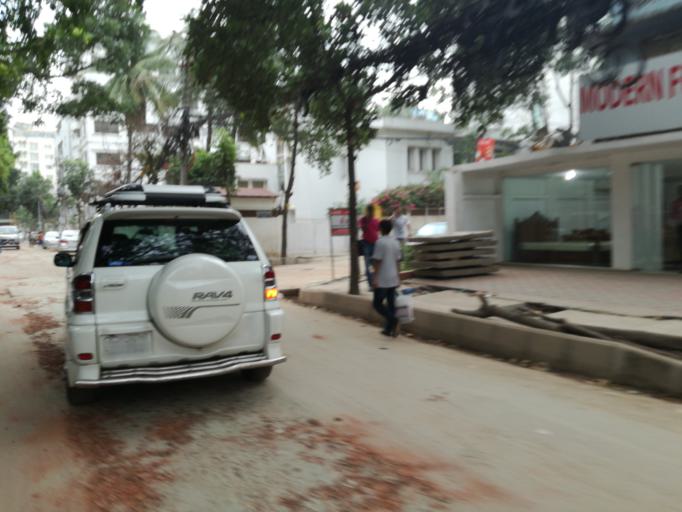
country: BD
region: Dhaka
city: Paltan
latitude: 23.7791
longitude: 90.4138
